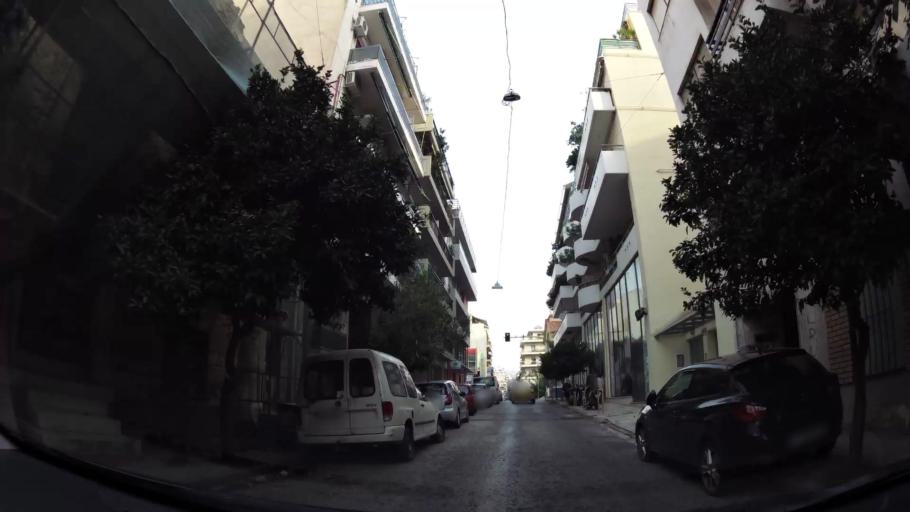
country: GR
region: Attica
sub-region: Nomarchia Athinas
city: Kipseli
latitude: 37.9906
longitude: 23.7461
